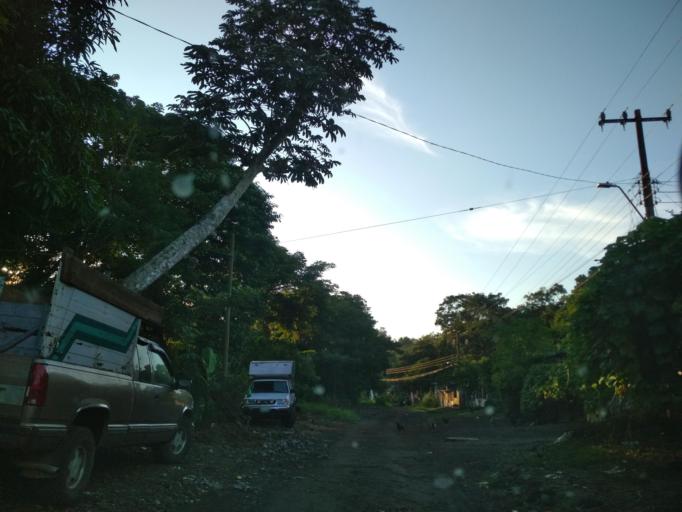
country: MX
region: Veracruz
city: Catemaco
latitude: 18.4209
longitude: -95.1257
